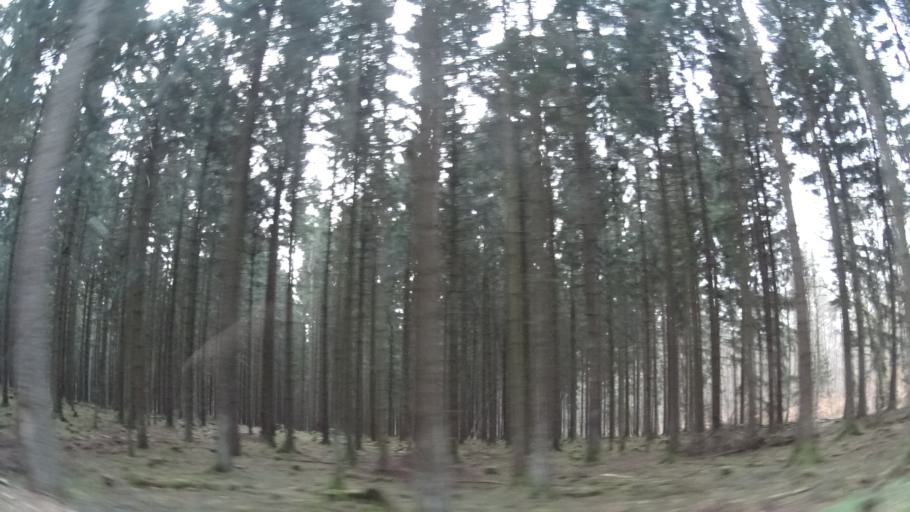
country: DE
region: Rheinland-Pfalz
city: Schwollen
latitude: 49.7212
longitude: 7.1739
